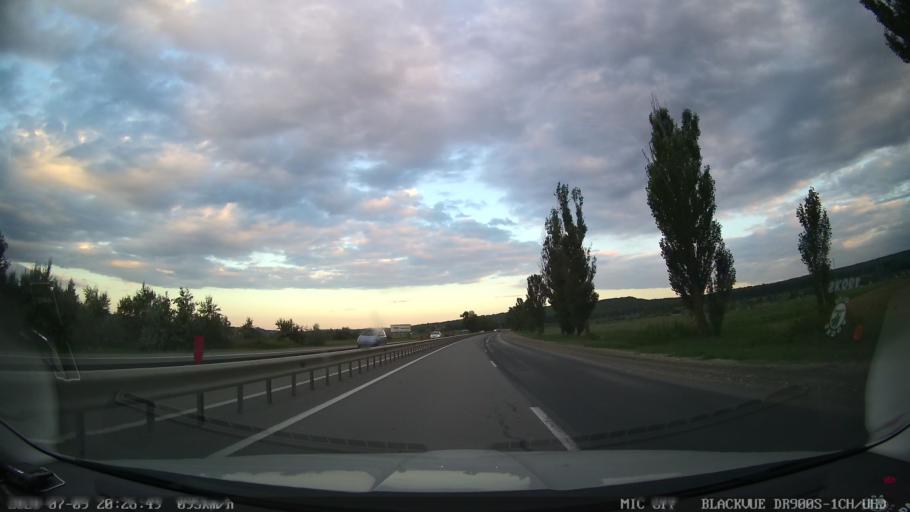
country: MD
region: Chisinau
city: Cricova
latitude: 47.1799
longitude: 28.7974
